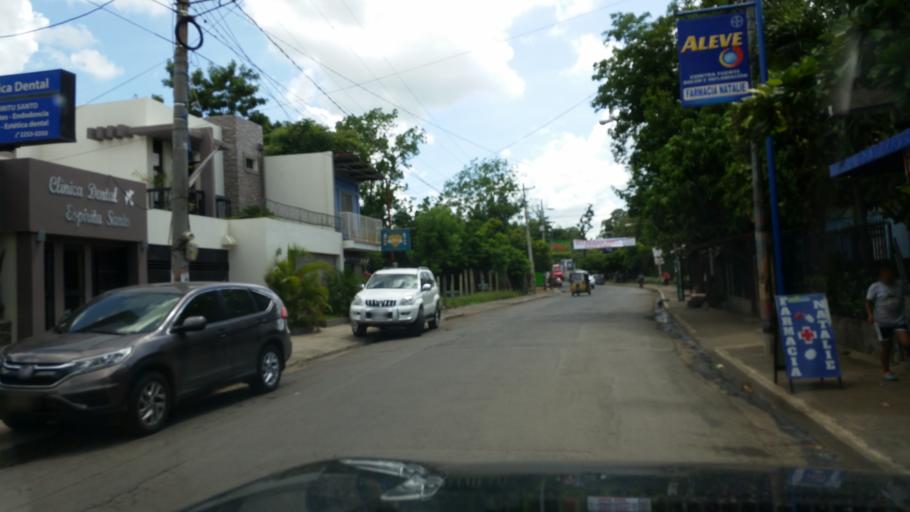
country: NI
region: Masaya
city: Ticuantepe
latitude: 12.0748
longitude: -86.2167
